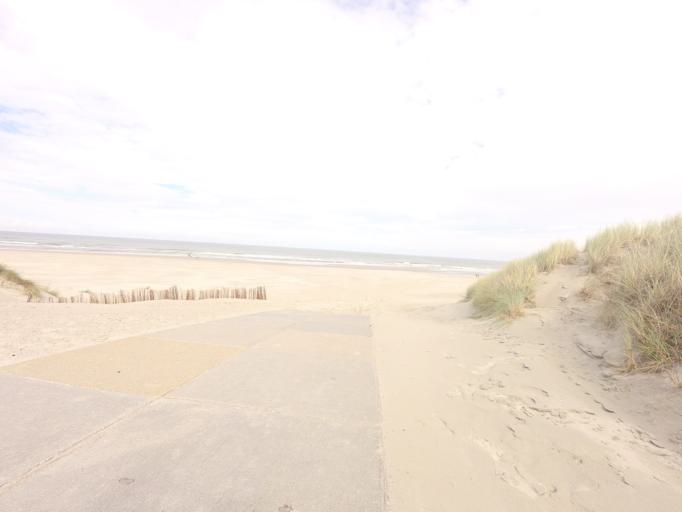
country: NL
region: Friesland
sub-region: Gemeente Ameland
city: Nes
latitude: 53.4628
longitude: 5.8350
